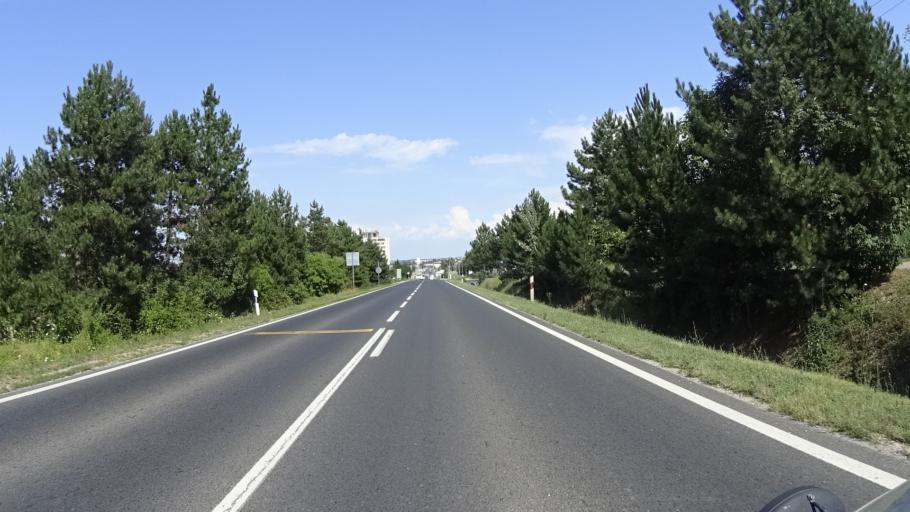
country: HU
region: Veszprem
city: Veszprem
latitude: 47.1132
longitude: 17.8772
